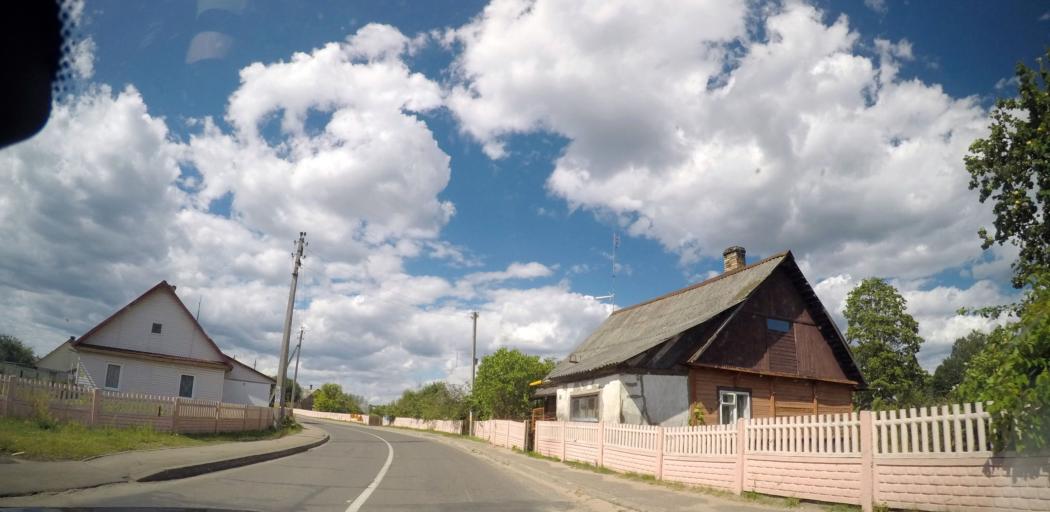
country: LT
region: Alytaus apskritis
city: Druskininkai
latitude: 53.8826
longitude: 24.1393
